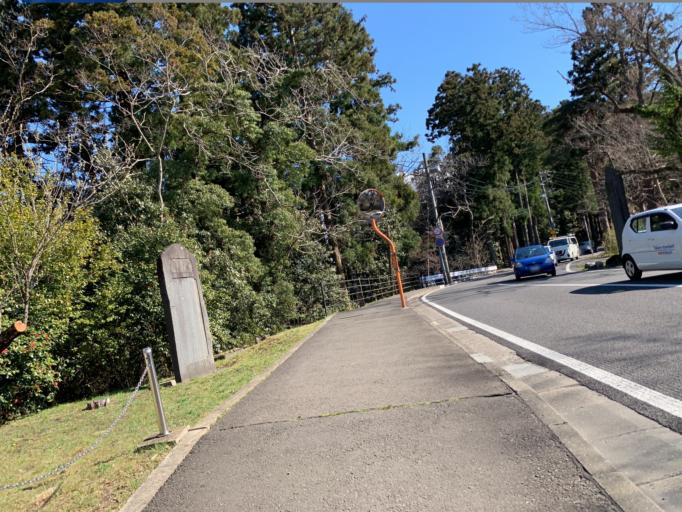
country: JP
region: Miyagi
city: Sendai
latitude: 38.2570
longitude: 140.8557
